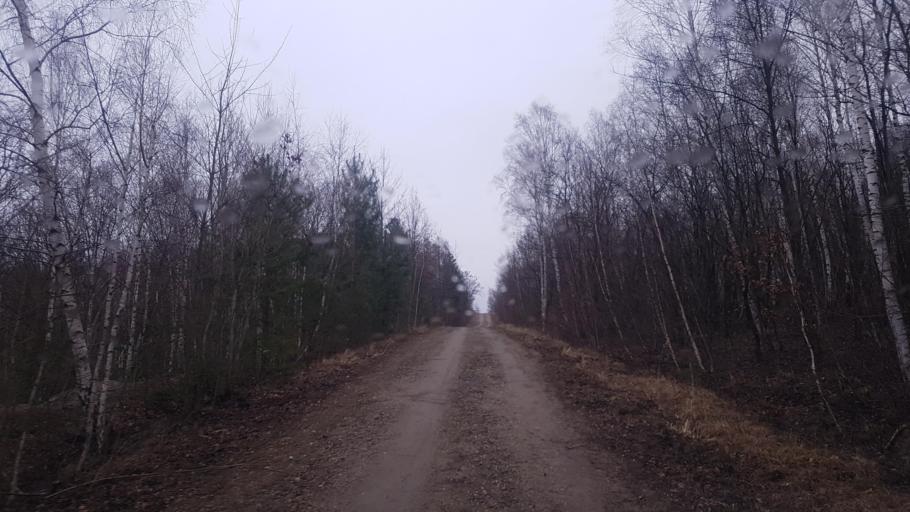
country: DE
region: Brandenburg
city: Schwarzheide
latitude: 51.4905
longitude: 13.8372
